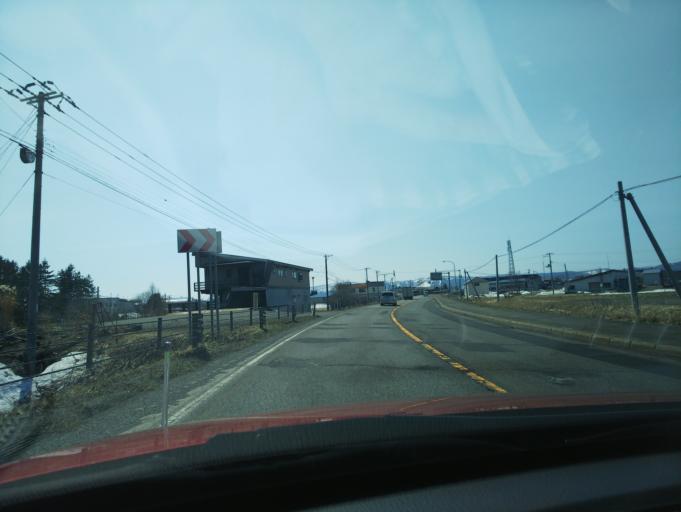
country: JP
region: Hokkaido
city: Nayoro
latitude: 44.2985
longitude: 142.4282
